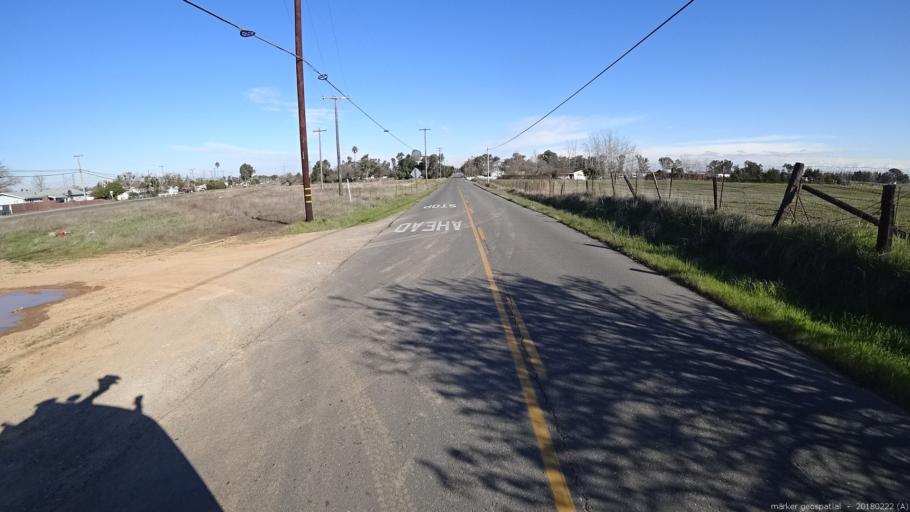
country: US
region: California
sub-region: Sacramento County
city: Elverta
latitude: 38.7215
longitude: -121.4668
